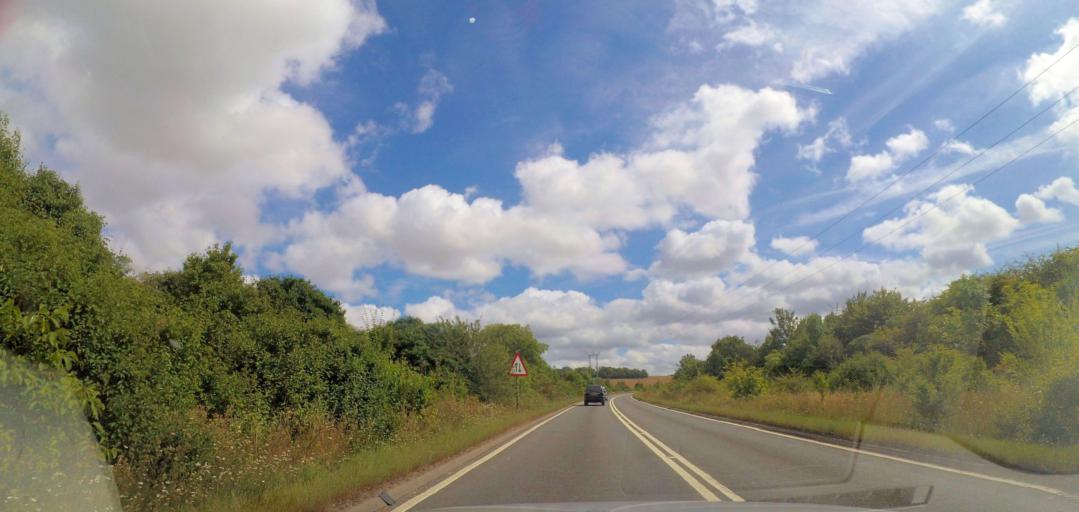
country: GB
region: England
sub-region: Hertfordshire
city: Royston
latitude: 52.0590
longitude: -0.0087
